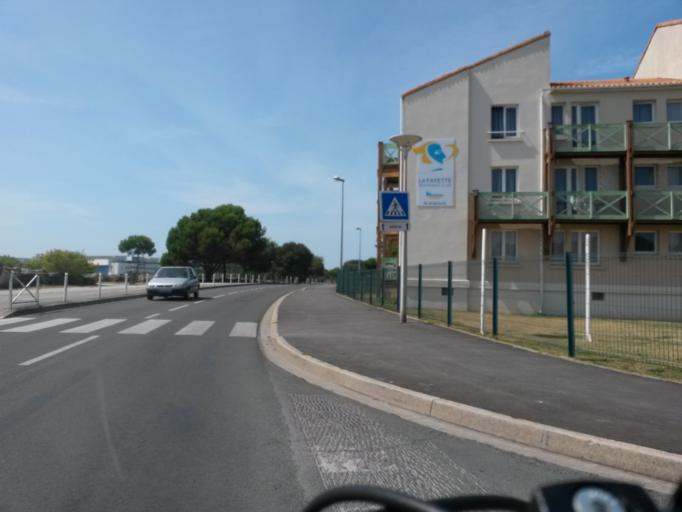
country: FR
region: Poitou-Charentes
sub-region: Departement de la Charente-Maritime
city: La Rochelle
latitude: 46.1538
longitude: -1.1841
